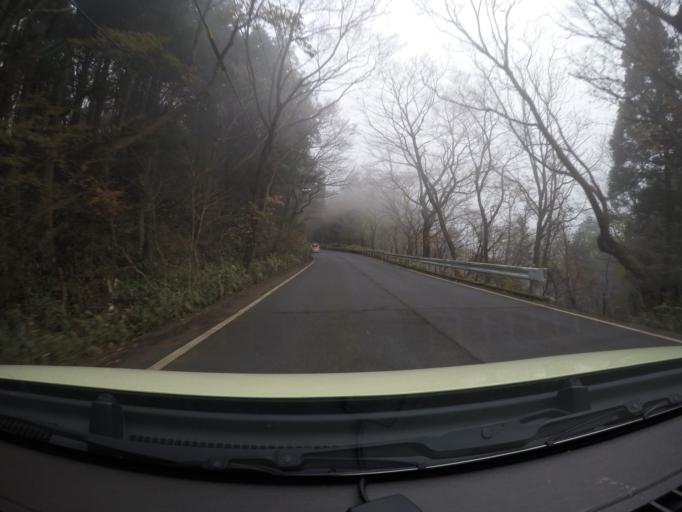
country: JP
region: Kanagawa
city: Hakone
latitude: 35.2464
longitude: 139.0162
